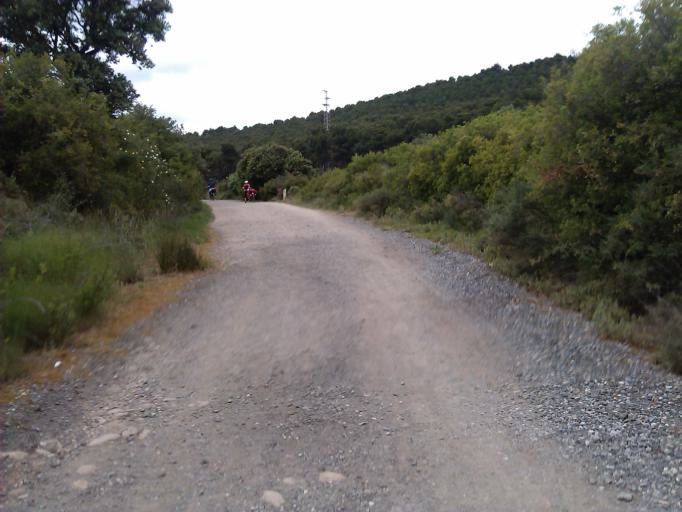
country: ES
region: La Rioja
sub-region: Provincia de La Rioja
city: Navarrete
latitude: 42.4399
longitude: -2.5232
